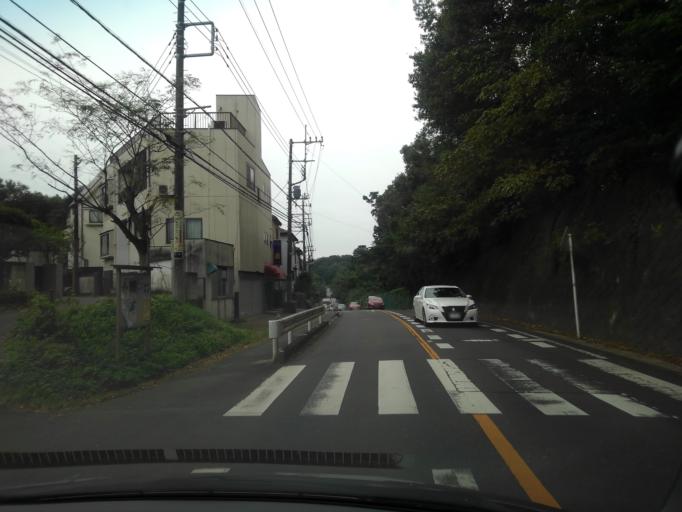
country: JP
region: Tokyo
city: Higashimurayama-shi
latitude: 35.7733
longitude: 139.4518
